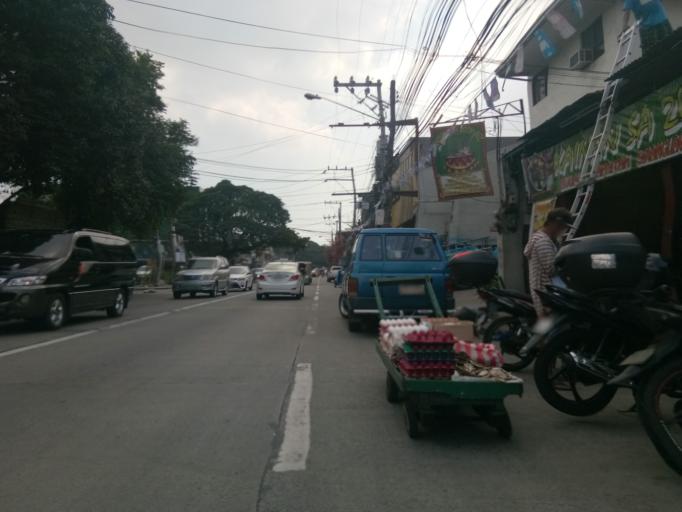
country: PH
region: Metro Manila
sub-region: Marikina
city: Calumpang
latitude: 14.6156
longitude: 121.0653
